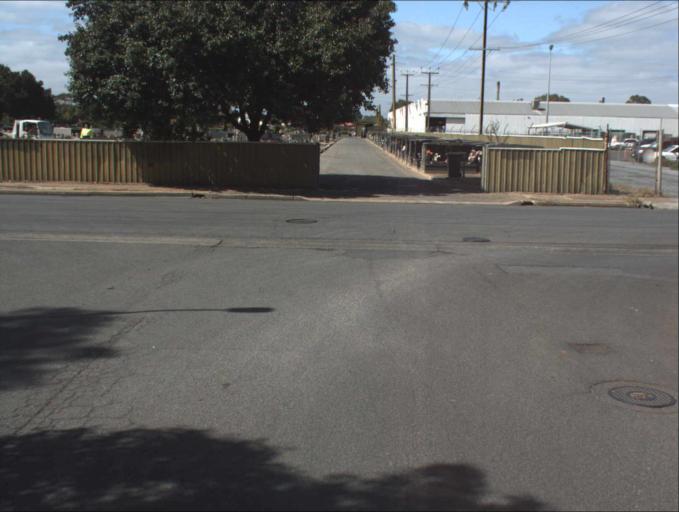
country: AU
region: South Australia
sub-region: Prospect
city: Prospect
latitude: -34.8819
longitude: 138.5811
